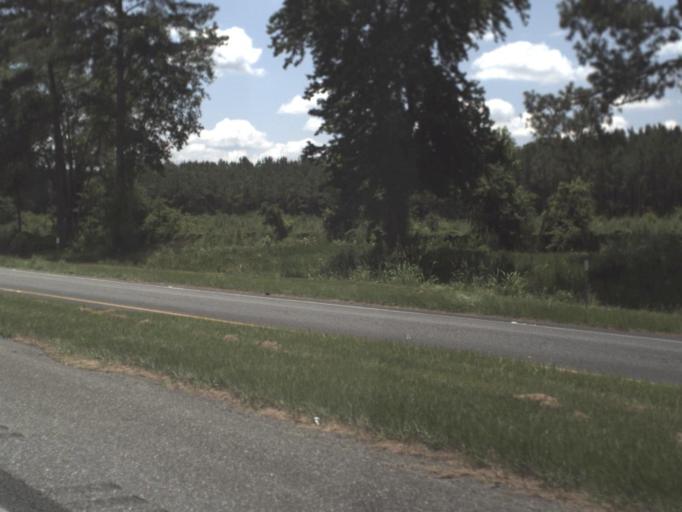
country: US
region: Florida
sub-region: Madison County
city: Madison
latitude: 30.4330
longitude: -83.6234
